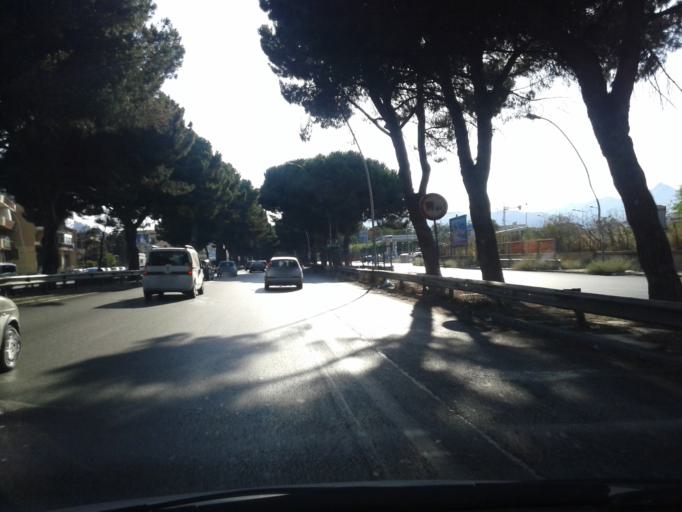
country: IT
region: Sicily
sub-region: Palermo
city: Ciaculli
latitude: 38.0900
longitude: 13.3737
